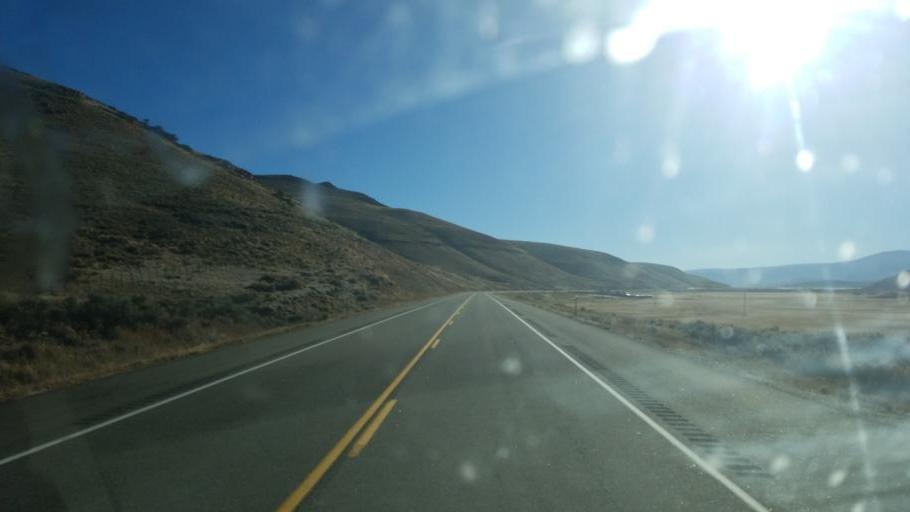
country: US
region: Colorado
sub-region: Gunnison County
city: Gunnison
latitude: 38.4876
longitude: -106.6835
